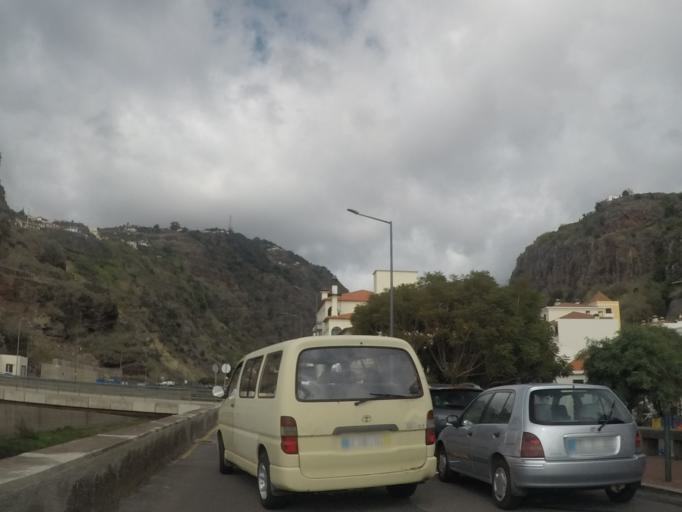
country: PT
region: Madeira
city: Ribeira Brava
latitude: 32.6712
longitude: -17.0653
